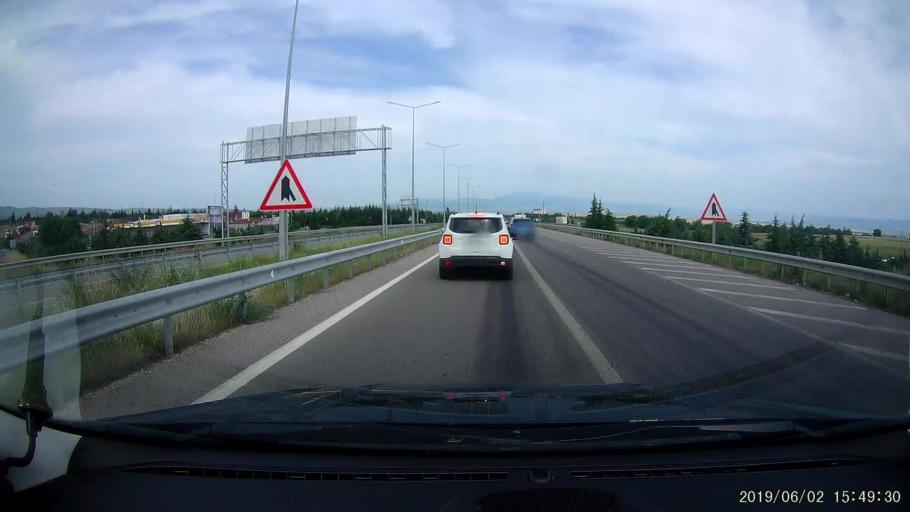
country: TR
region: Amasya
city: Merzifon
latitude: 40.8575
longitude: 35.4636
